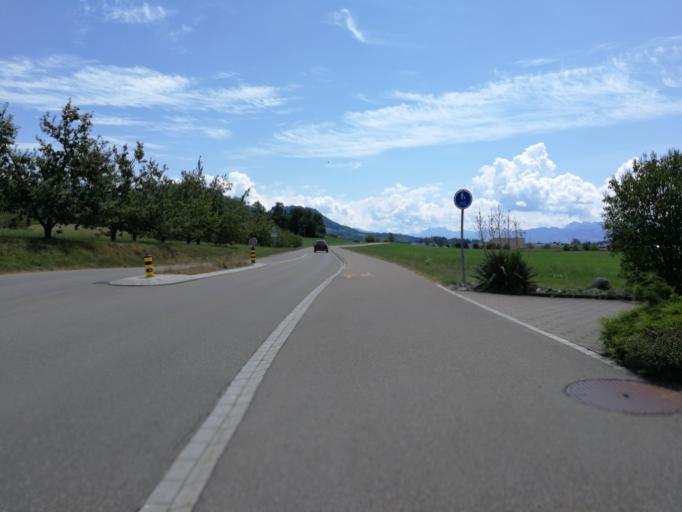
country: CH
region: Zurich
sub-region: Bezirk Hinwil
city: Hinwil
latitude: 47.3106
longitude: 8.8268
